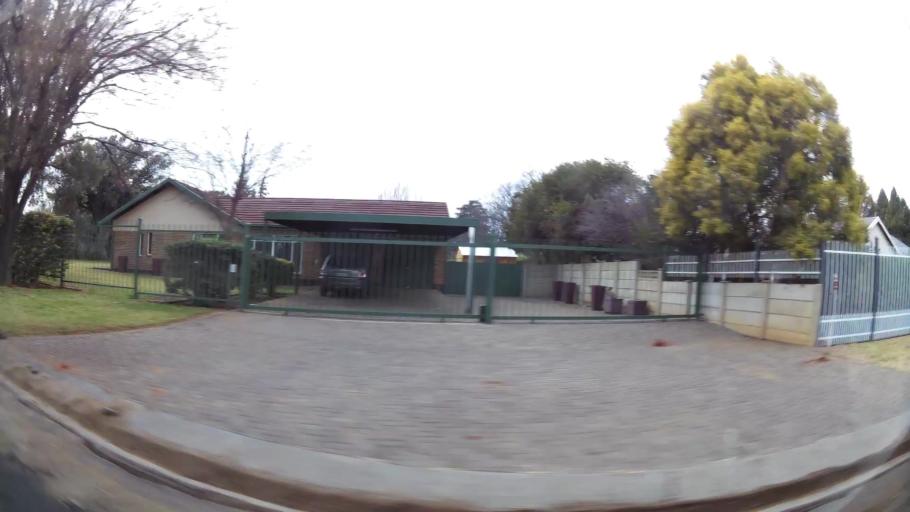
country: ZA
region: Orange Free State
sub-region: Mangaung Metropolitan Municipality
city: Bloemfontein
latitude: -29.1176
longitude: 26.1651
